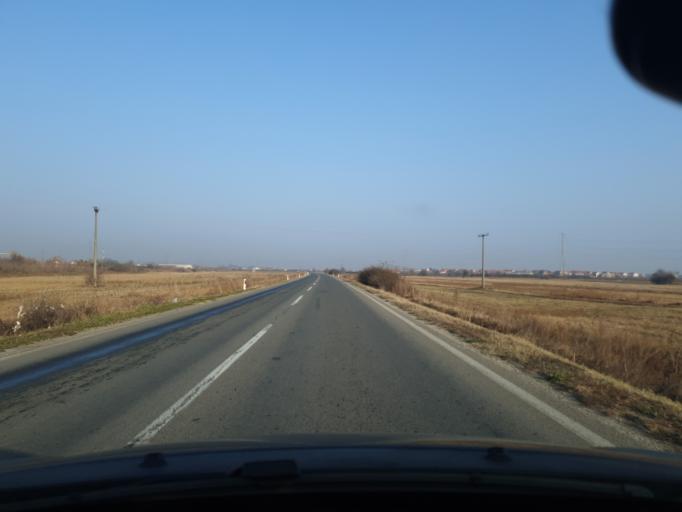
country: RS
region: Central Serbia
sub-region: Jablanicki Okrug
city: Leskovac
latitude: 42.9874
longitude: 21.9736
